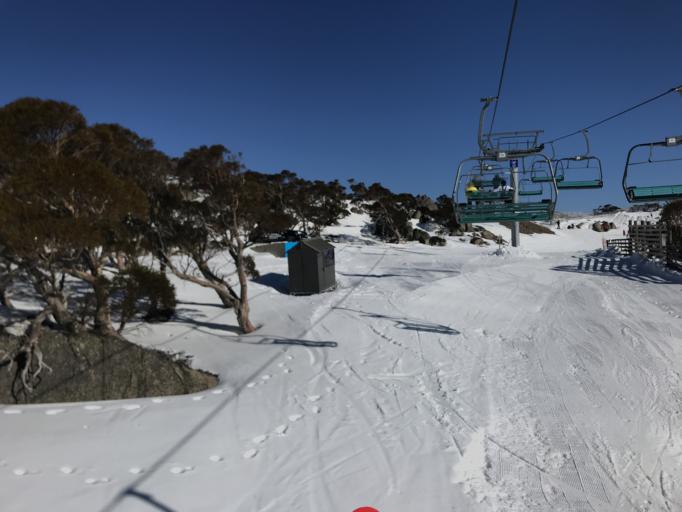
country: AU
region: New South Wales
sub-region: Snowy River
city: Jindabyne
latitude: -36.3859
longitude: 148.3944
